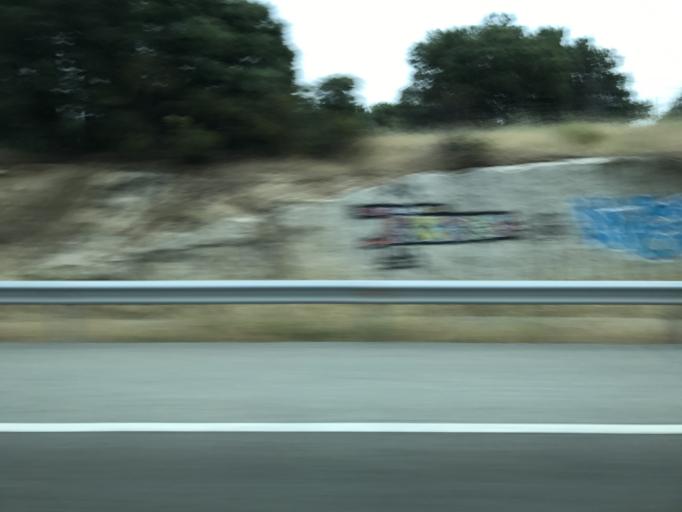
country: ES
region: Madrid
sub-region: Provincia de Madrid
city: La Cabrera
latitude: 40.8543
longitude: -3.6109
